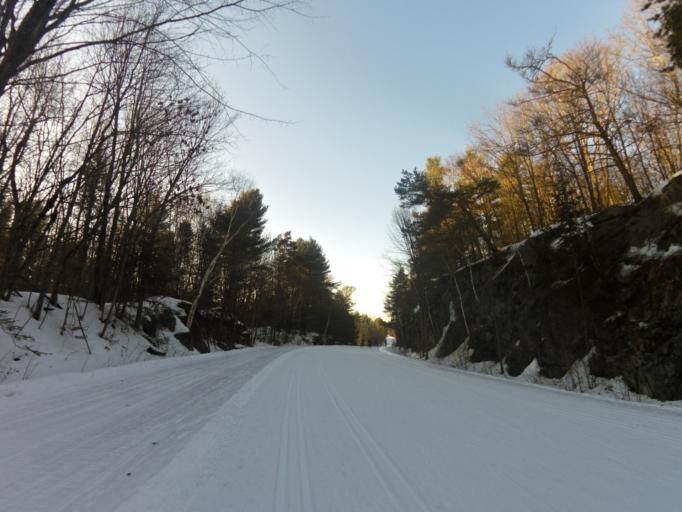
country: CA
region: Quebec
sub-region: Outaouais
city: Gatineau
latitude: 45.5163
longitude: -75.8268
